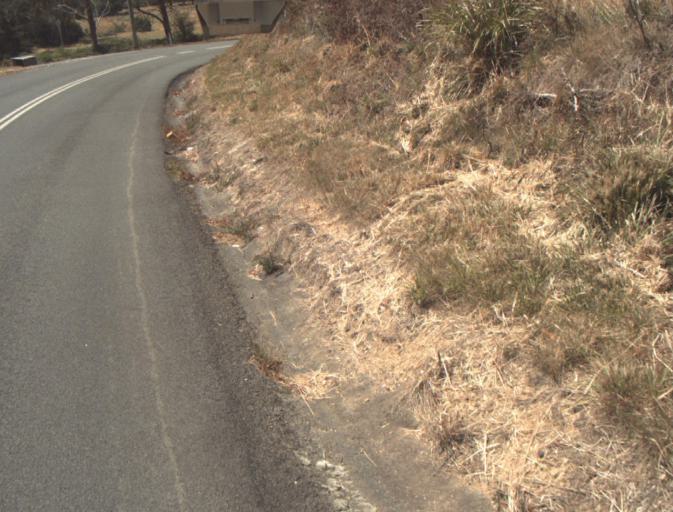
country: AU
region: Tasmania
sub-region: Launceston
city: Mayfield
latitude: -41.2666
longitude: 147.1295
